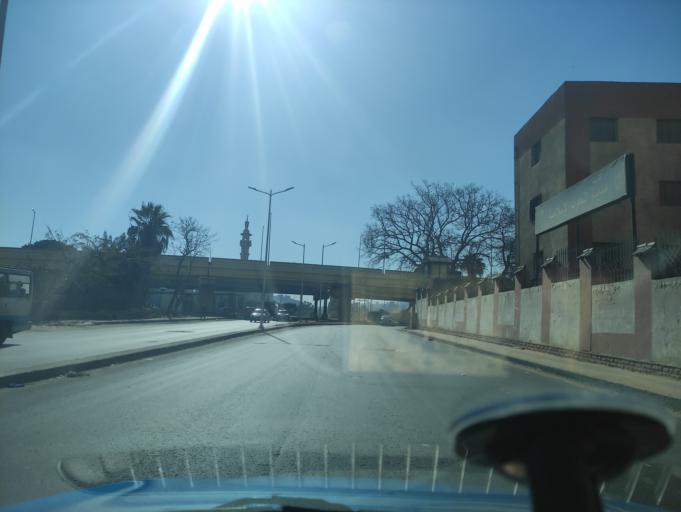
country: EG
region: Muhafazat al Qahirah
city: Cairo
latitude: 30.0564
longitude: 31.2791
